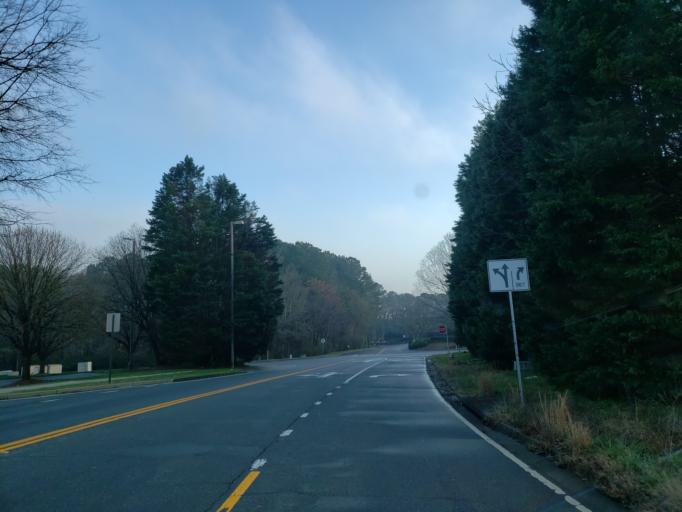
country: US
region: Georgia
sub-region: Cobb County
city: Kennesaw
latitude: 34.0050
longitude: -84.5940
